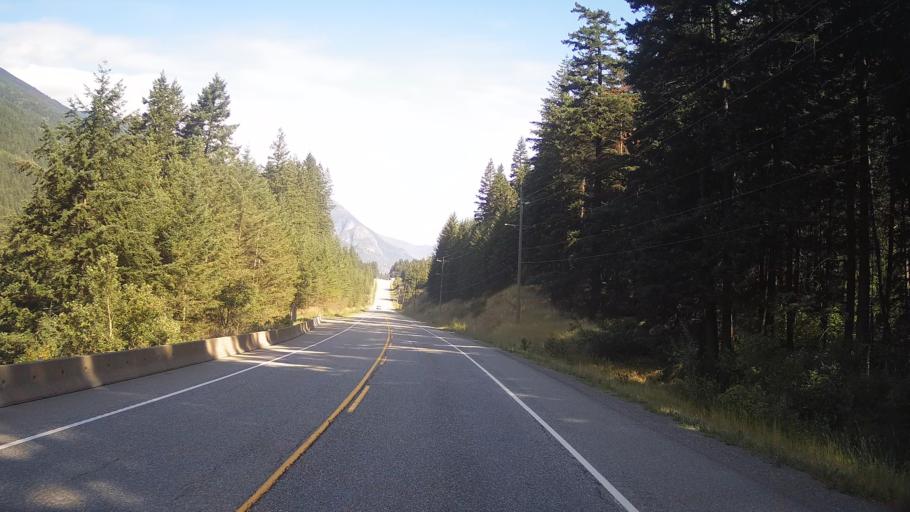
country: CA
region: British Columbia
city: Hope
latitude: 50.0273
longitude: -121.5281
